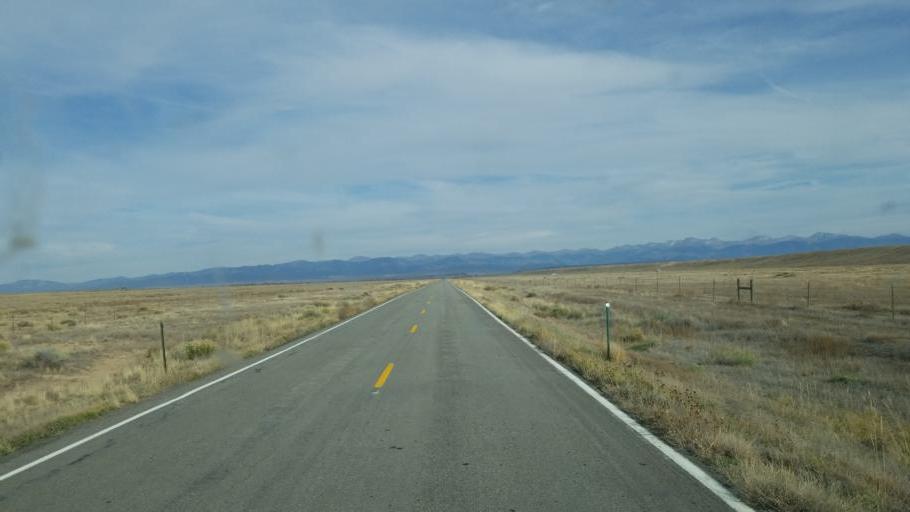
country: US
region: Colorado
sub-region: Costilla County
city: San Luis
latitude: 37.1813
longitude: -105.6193
